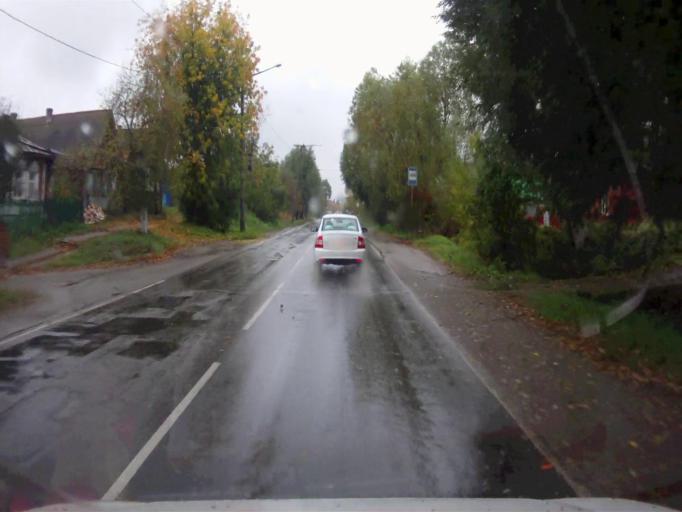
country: RU
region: Chelyabinsk
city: Kyshtym
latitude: 55.7207
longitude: 60.5417
